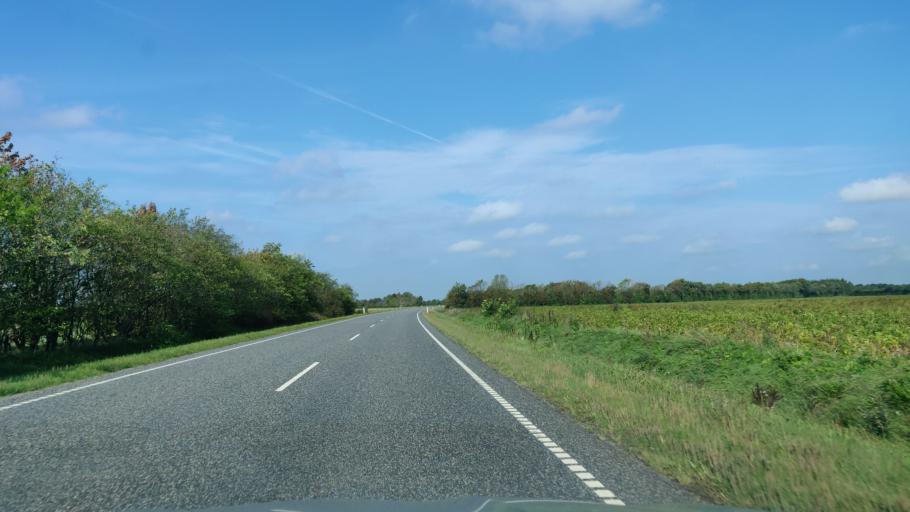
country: DK
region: Central Jutland
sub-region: Herning Kommune
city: Sunds
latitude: 56.2474
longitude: 9.0674
